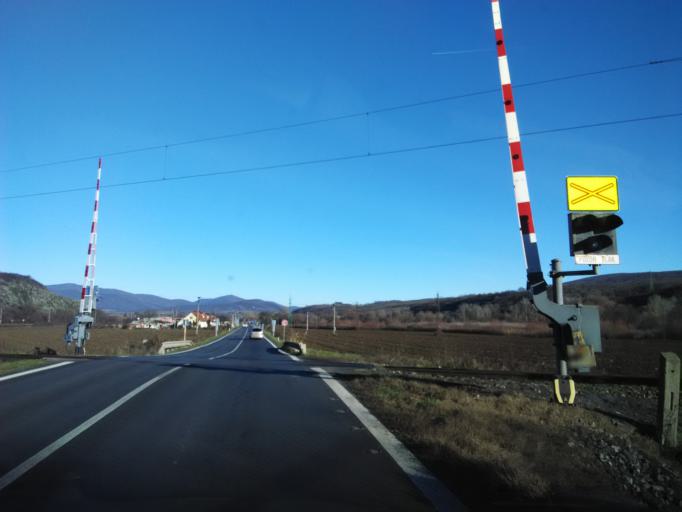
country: SK
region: Nitriansky
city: Tlmace
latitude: 48.3003
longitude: 18.5316
